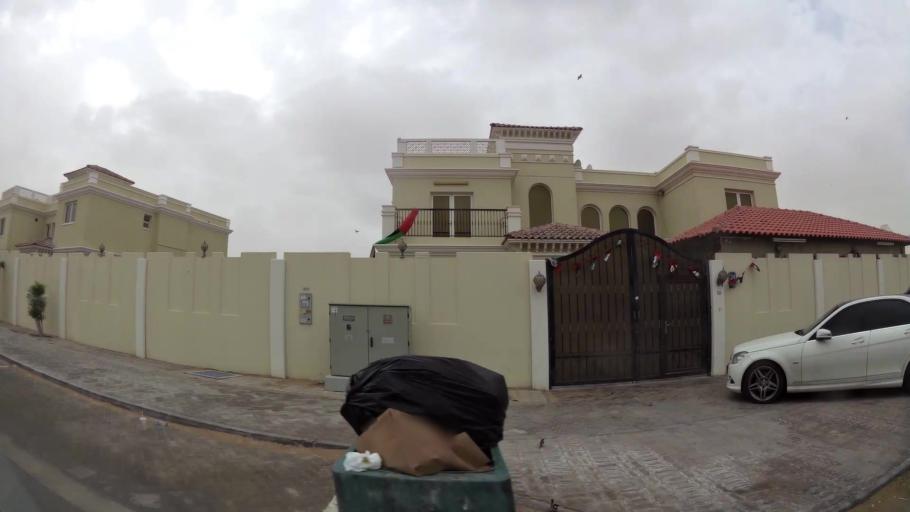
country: AE
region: Abu Dhabi
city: Abu Dhabi
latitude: 24.4473
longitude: 54.7140
